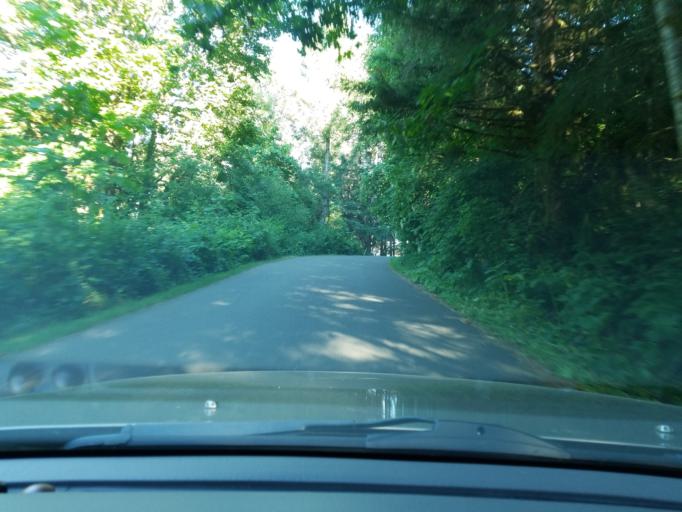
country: US
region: Oregon
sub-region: Yamhill County
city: McMinnville
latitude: 45.2256
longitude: -123.2695
